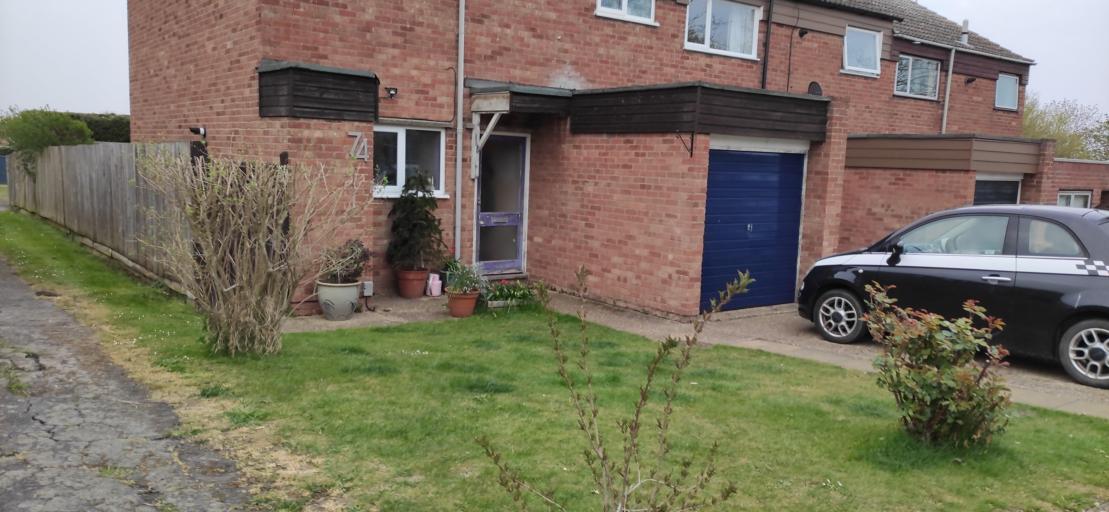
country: GB
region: England
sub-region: Cambridgeshire
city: Swavesey
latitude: 52.2509
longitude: 0.0152
